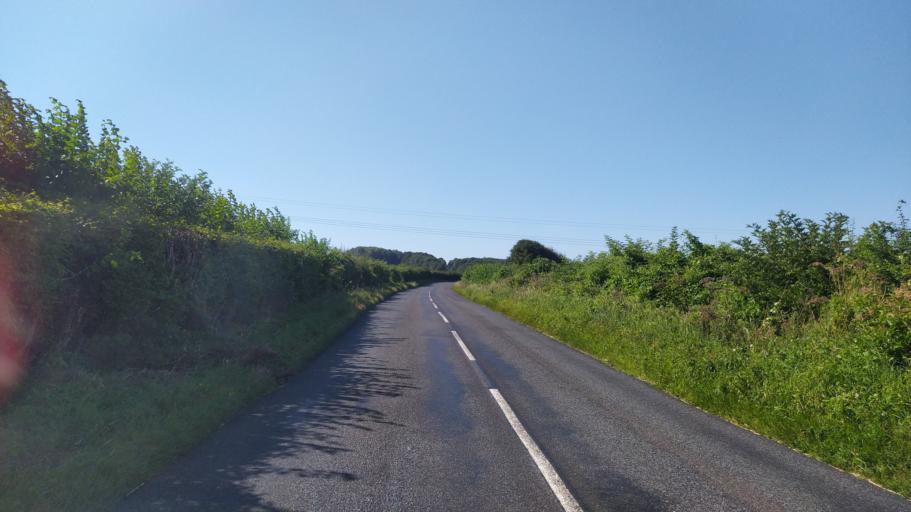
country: GB
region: England
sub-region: Dorset
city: Lytchett Matravers
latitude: 50.7712
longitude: -2.1274
